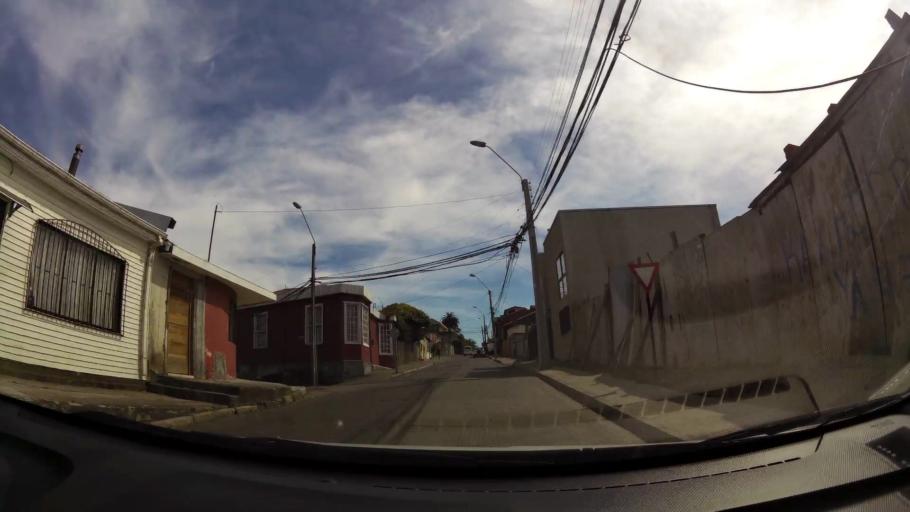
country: CL
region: Biobio
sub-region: Provincia de Concepcion
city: Talcahuano
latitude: -36.7189
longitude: -73.1109
